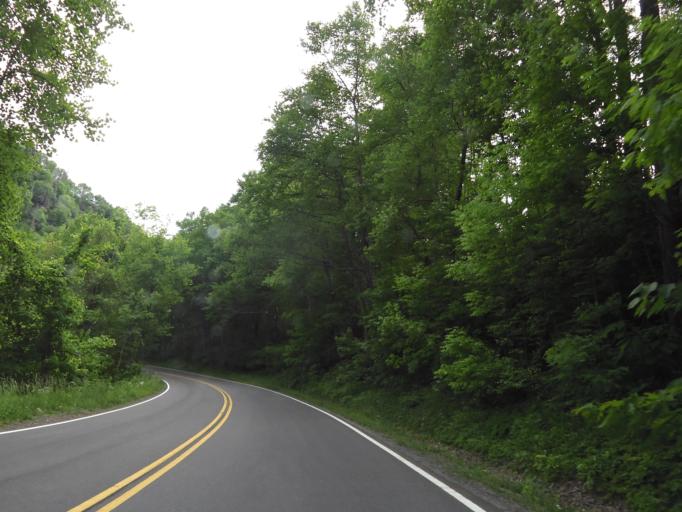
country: US
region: Tennessee
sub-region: Sevier County
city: Gatlinburg
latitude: 35.6374
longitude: -83.4654
